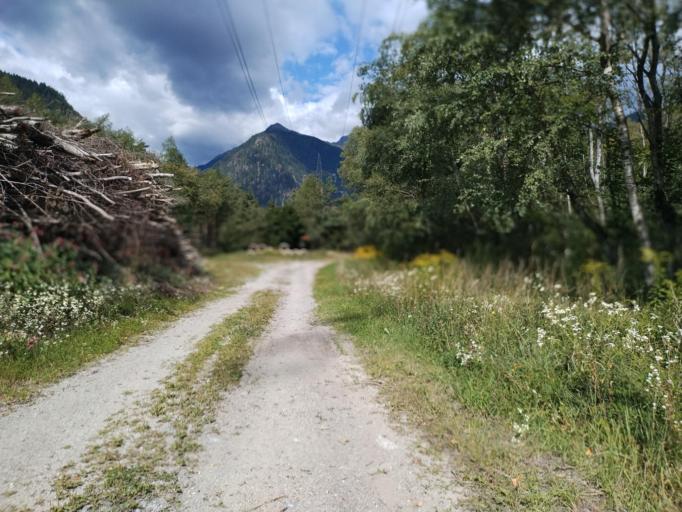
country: AT
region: Tyrol
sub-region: Politischer Bezirk Lienz
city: Hopfgarten in Defereggen
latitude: 46.9220
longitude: 12.5975
